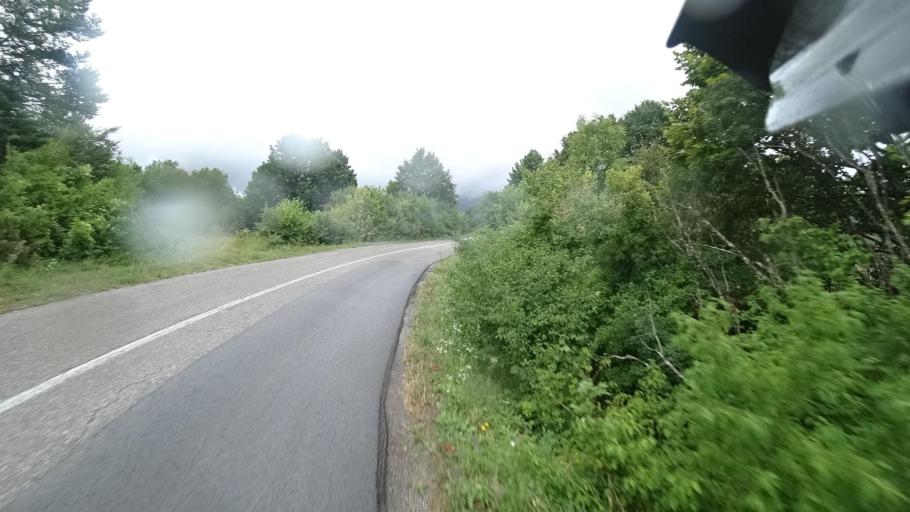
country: HR
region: Karlovacka
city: Plaski
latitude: 45.0251
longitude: 15.4143
